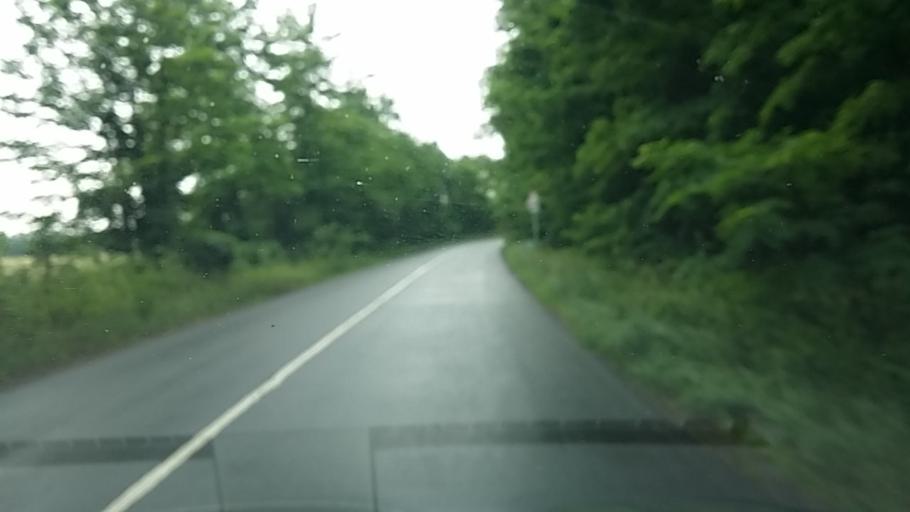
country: HU
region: Pest
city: Szob
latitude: 47.9461
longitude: 18.7808
